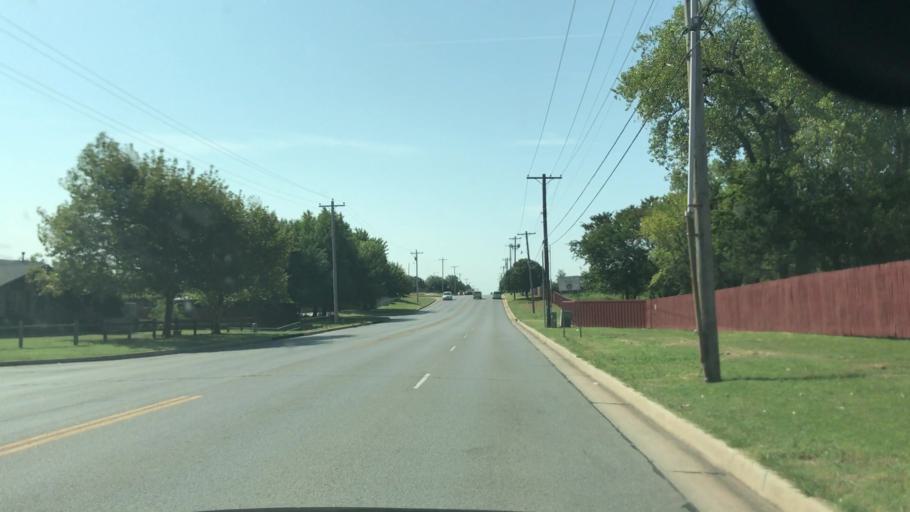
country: US
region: Oklahoma
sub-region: Cleveland County
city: Moore
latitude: 35.3575
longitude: -97.5122
